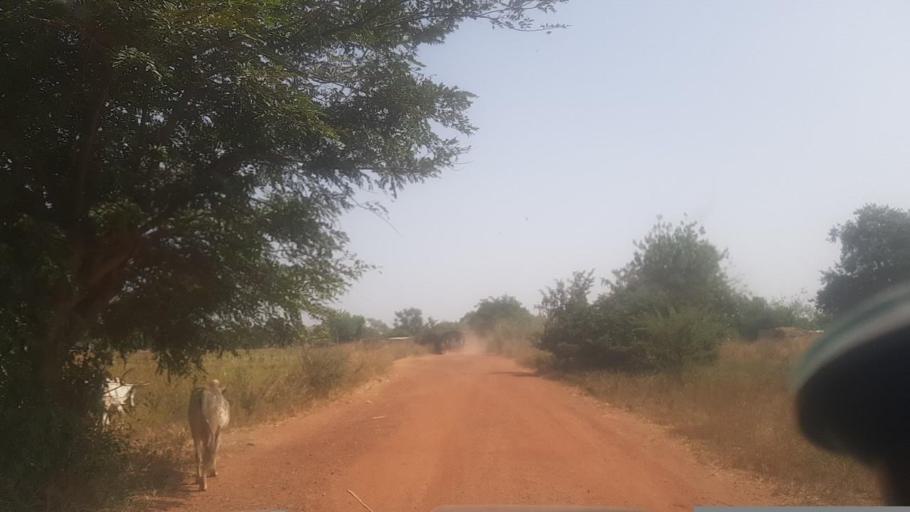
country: ML
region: Segou
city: Bla
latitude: 12.9138
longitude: -6.2484
